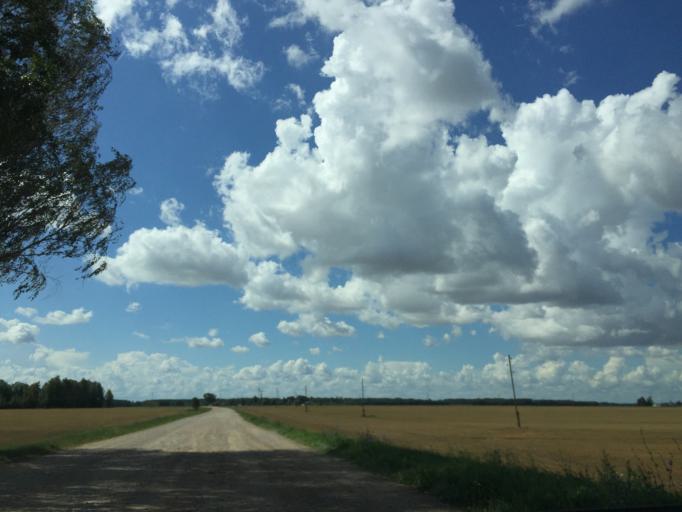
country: LV
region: Rundales
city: Pilsrundale
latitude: 56.3834
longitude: 24.0837
